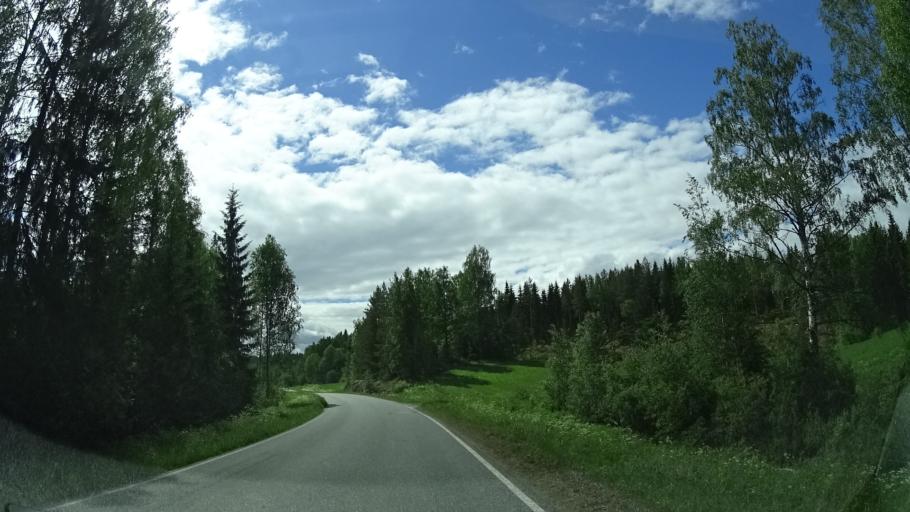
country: FI
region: Central Finland
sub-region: Joutsa
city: Luhanka
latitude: 61.7871
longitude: 25.6463
